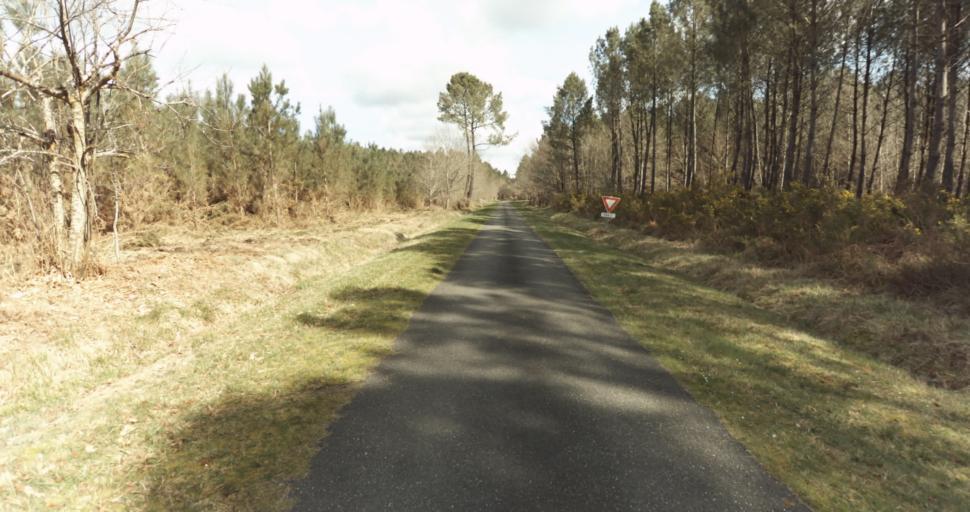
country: FR
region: Aquitaine
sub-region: Departement des Landes
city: Roquefort
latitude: 44.0630
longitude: -0.3358
